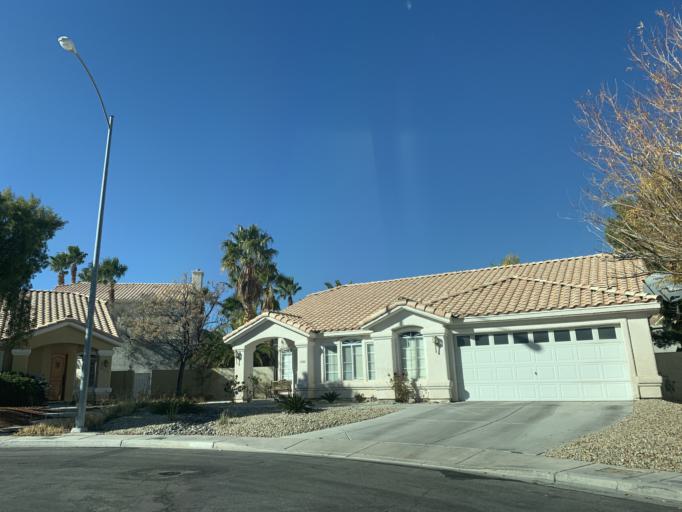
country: US
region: Nevada
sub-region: Clark County
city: Summerlin South
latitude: 36.1235
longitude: -115.2865
